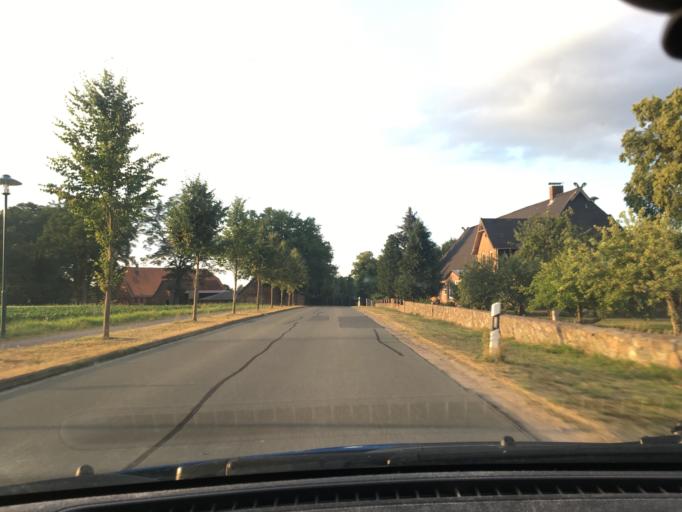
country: DE
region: Lower Saxony
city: Eyendorf
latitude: 53.1936
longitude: 10.1911
